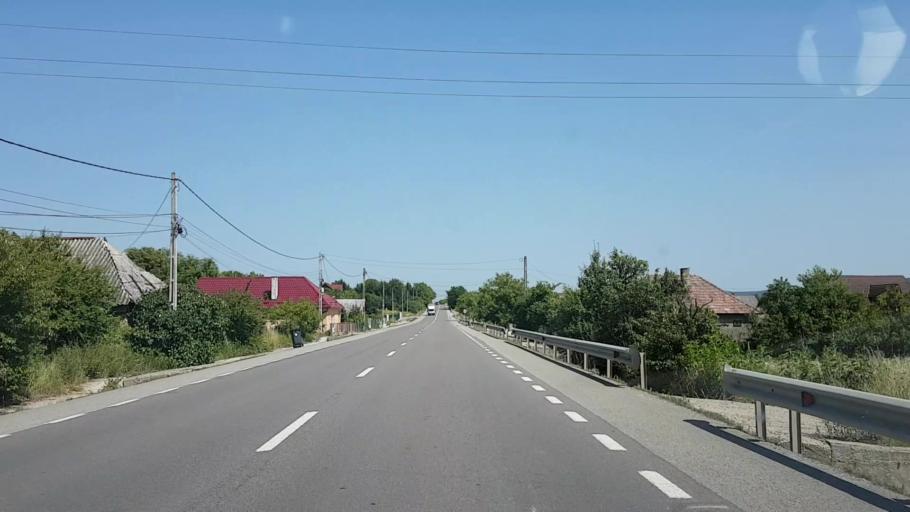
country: RO
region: Bistrita-Nasaud
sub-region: Comuna Uriu
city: Cristestii Ciceului
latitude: 47.1862
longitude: 24.1210
